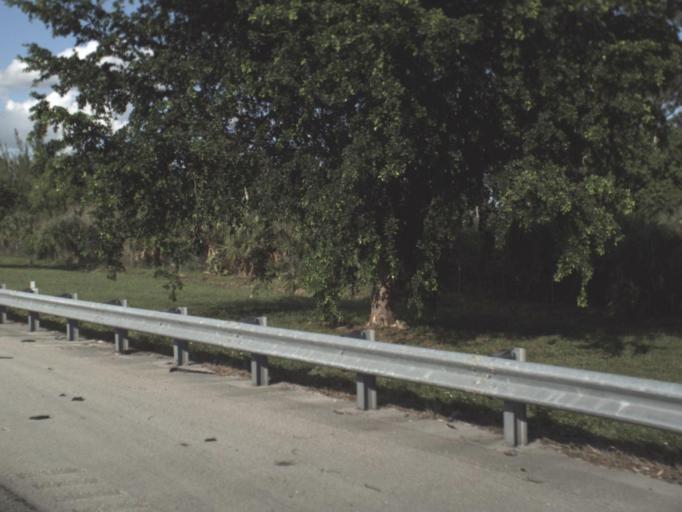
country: US
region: Florida
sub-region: Palm Beach County
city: Boca Pointe
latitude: 26.3094
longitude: -80.1696
